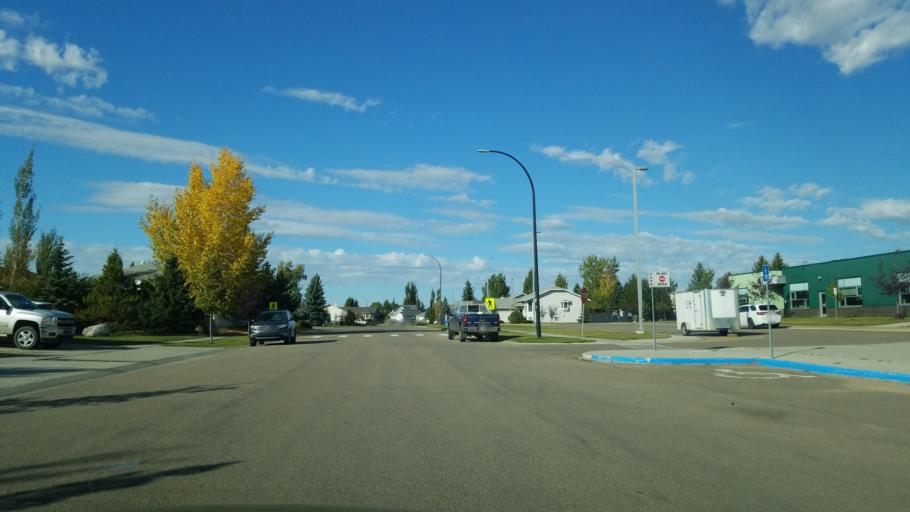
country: CA
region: Saskatchewan
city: Lloydminster
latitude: 53.2558
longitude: -110.0214
